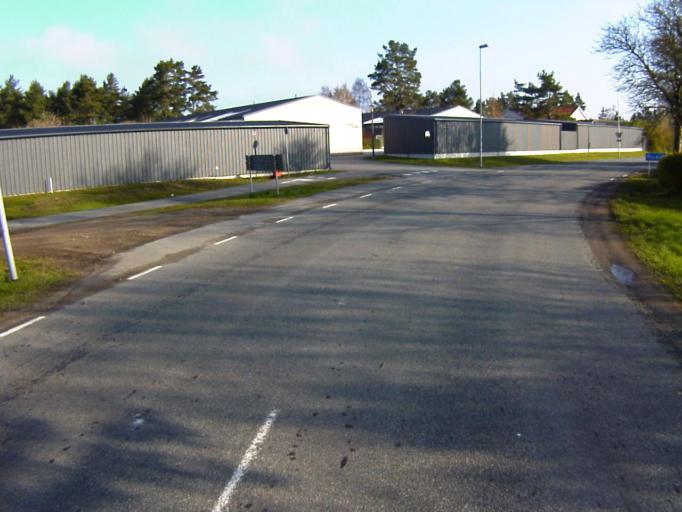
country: SE
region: Skane
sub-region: Kristianstads Kommun
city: Norra Asum
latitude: 56.0032
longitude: 14.0958
